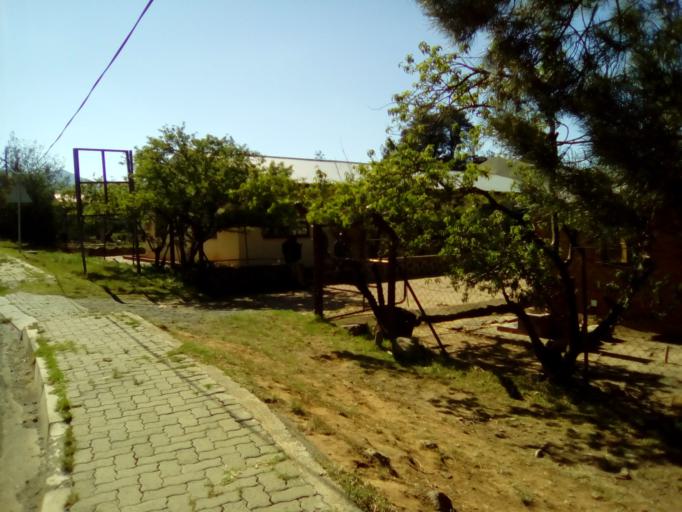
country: LS
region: Qacha's Nek
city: Qacha's Nek
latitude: -30.1096
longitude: 28.6823
